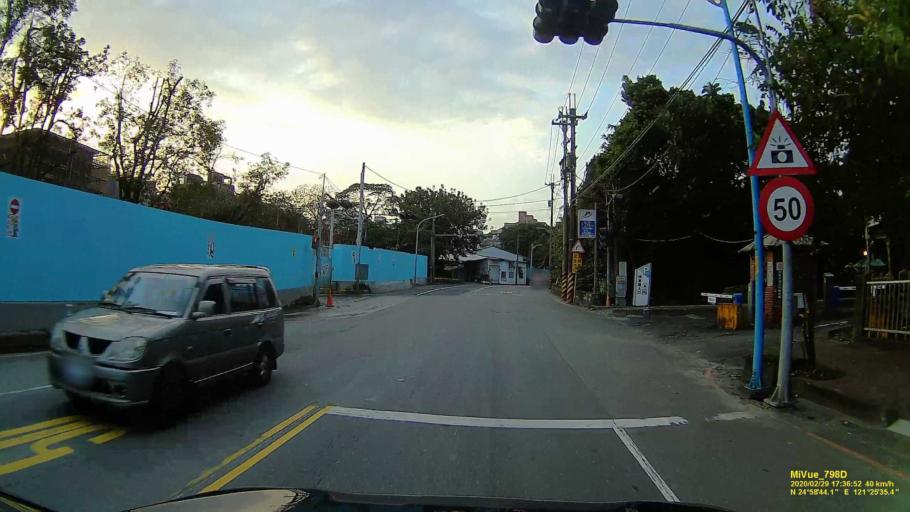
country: TW
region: Taipei
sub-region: Taipei
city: Banqiao
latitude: 24.9792
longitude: 121.4263
